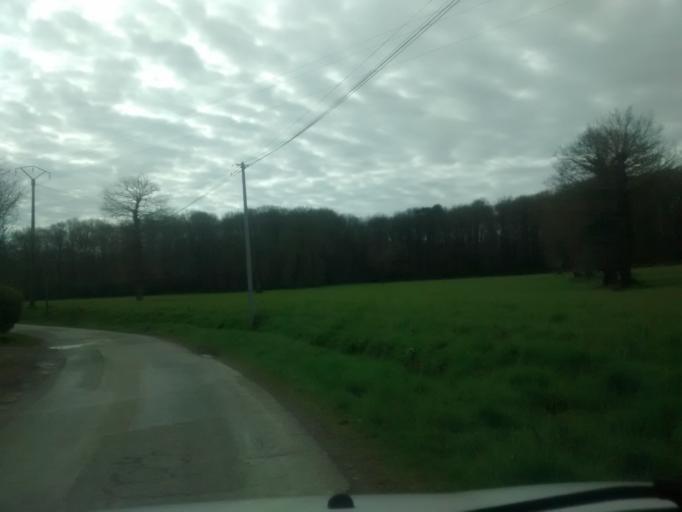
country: FR
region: Brittany
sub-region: Departement d'Ille-et-Vilaine
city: Chasne-sur-Illet
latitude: 48.2322
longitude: -1.5431
